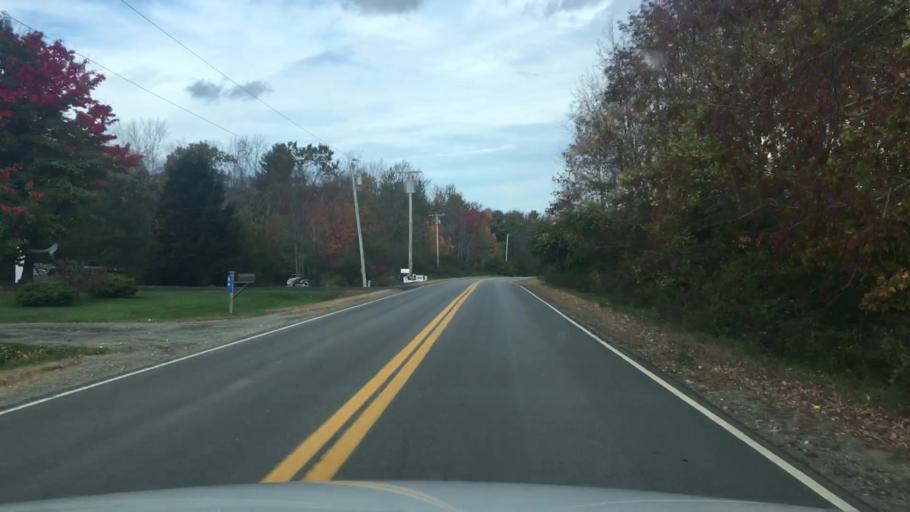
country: US
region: Maine
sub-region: Waldo County
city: Searsmont
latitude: 44.3988
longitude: -69.1350
